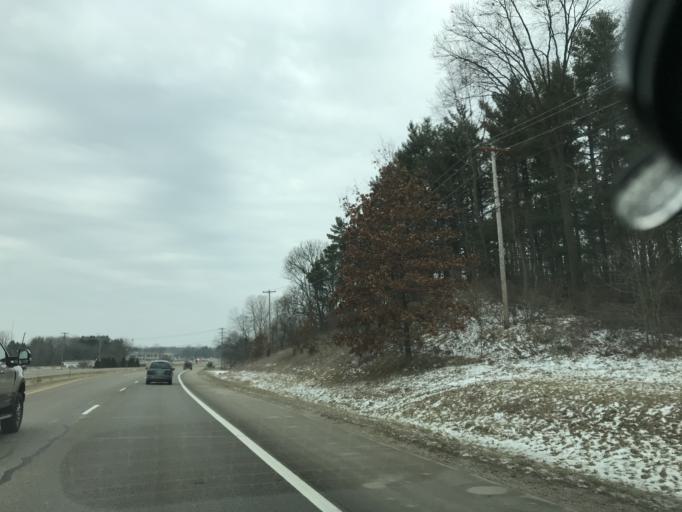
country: US
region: Michigan
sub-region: Kent County
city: Rockford
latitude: 43.0770
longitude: -85.5693
